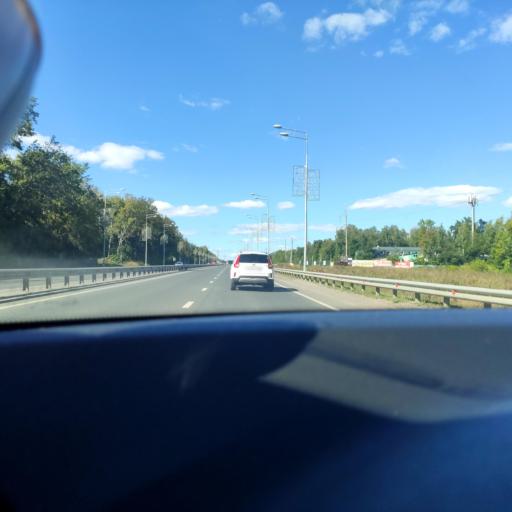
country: RU
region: Samara
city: Novosemeykino
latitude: 53.3385
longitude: 50.2331
